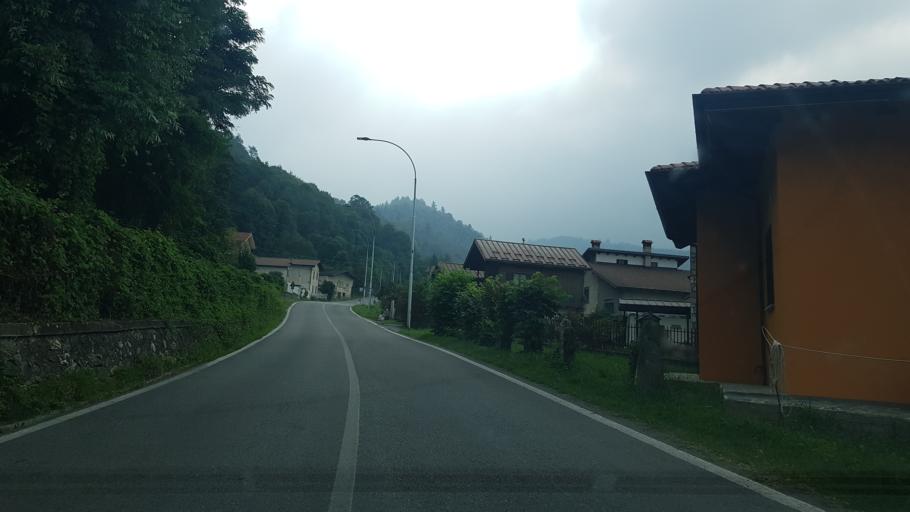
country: IT
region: Piedmont
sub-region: Provincia di Cuneo
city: Chiusa di Pesio
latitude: 44.3205
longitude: 7.6844
